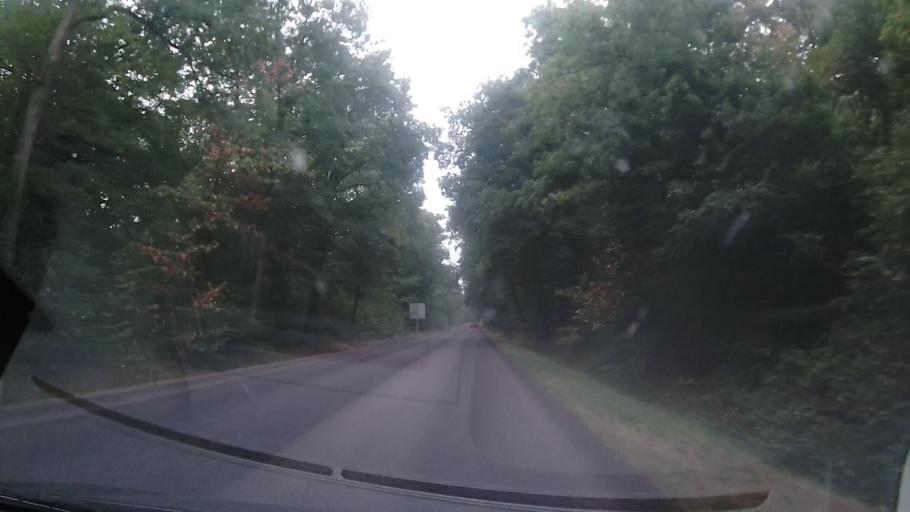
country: FR
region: Ile-de-France
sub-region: Departement de l'Essonne
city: Dourdan
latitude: 48.5459
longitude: 1.9875
